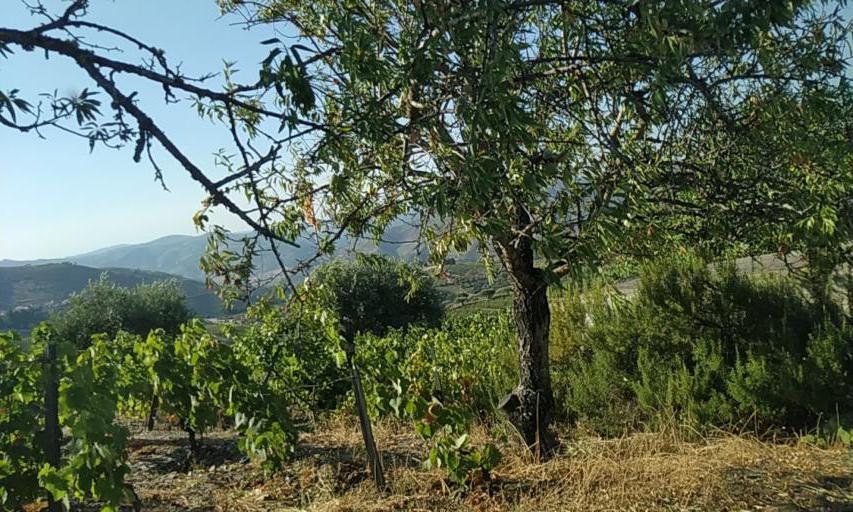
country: PT
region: Viseu
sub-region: Sao Joao da Pesqueira
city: Sao Joao da Pesqueira
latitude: 41.1788
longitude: -7.4045
